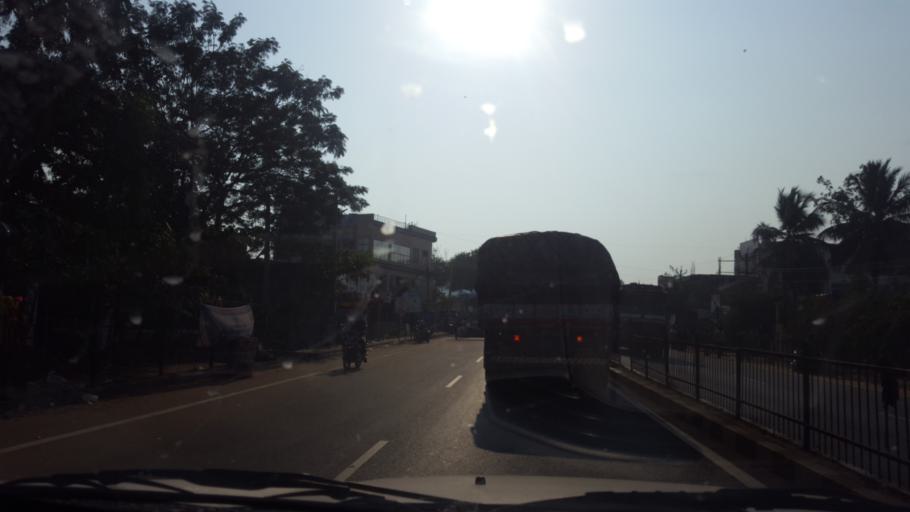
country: IN
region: Andhra Pradesh
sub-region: Vishakhapatnam
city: Etikoppaka
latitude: 17.4092
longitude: 82.7163
